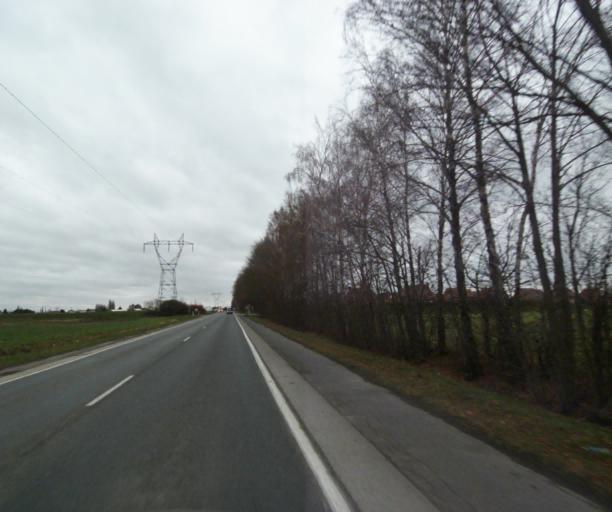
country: FR
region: Nord-Pas-de-Calais
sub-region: Departement du Nord
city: Marly
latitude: 50.3513
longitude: 3.5578
